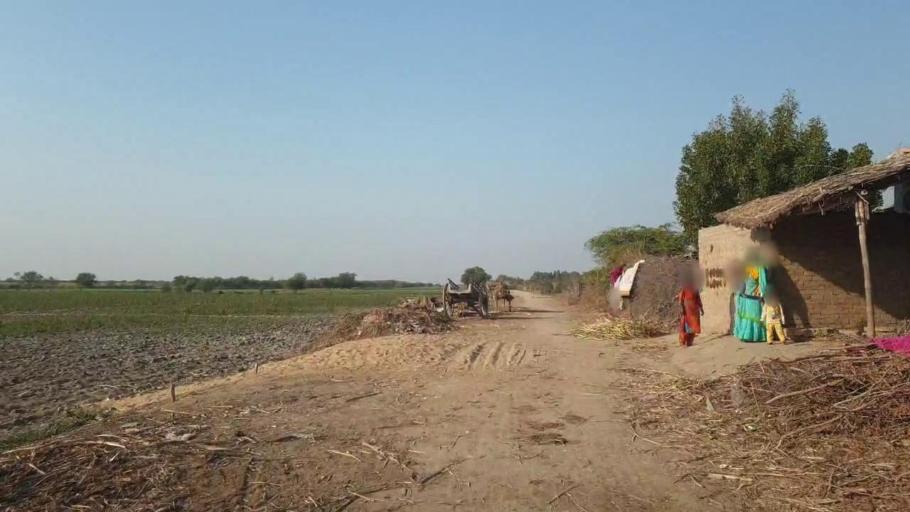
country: PK
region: Sindh
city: Mirpur Khas
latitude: 25.4414
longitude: 68.9355
